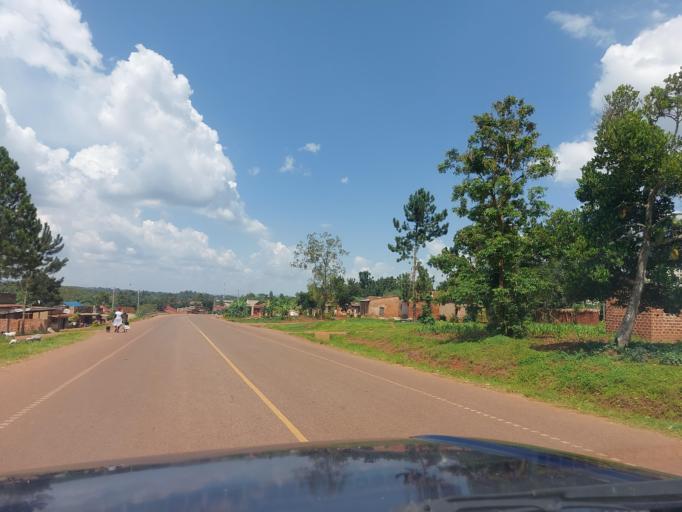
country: UG
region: Central Region
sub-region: Buikwe District
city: Njeru
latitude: 0.3863
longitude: 33.1623
